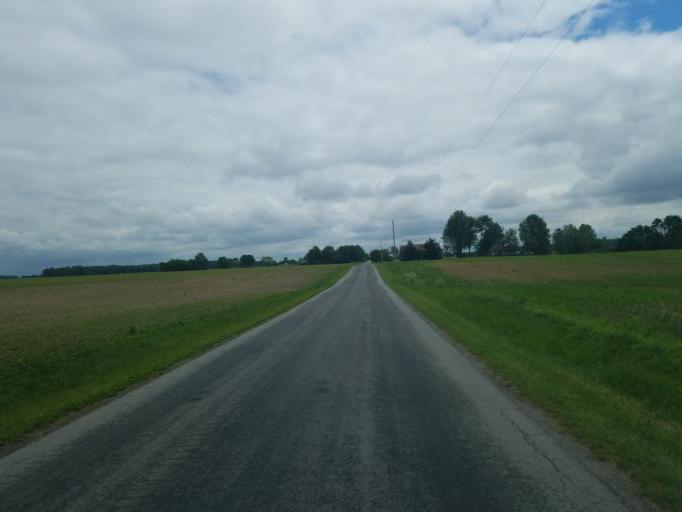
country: US
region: Ohio
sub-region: Crawford County
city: Bucyrus
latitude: 40.7750
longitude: -83.1230
